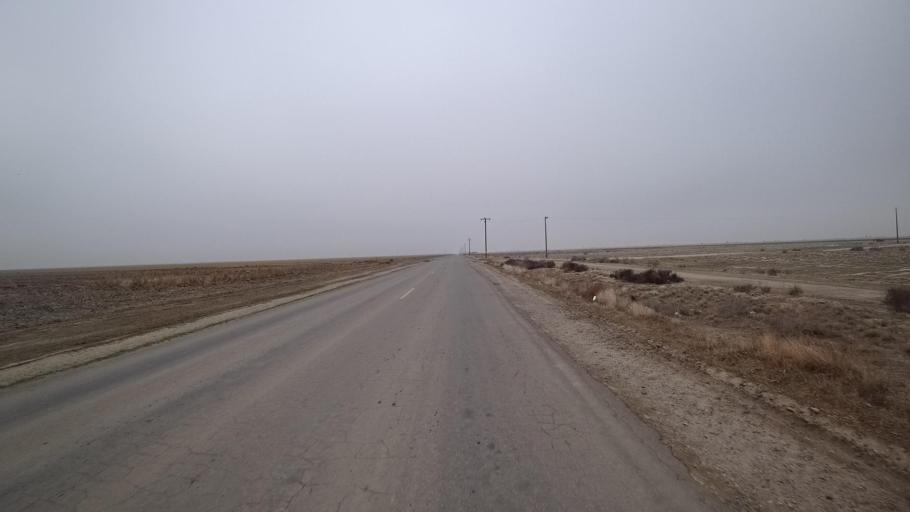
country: US
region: California
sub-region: Kern County
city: Rosedale
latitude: 35.2317
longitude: -119.2328
